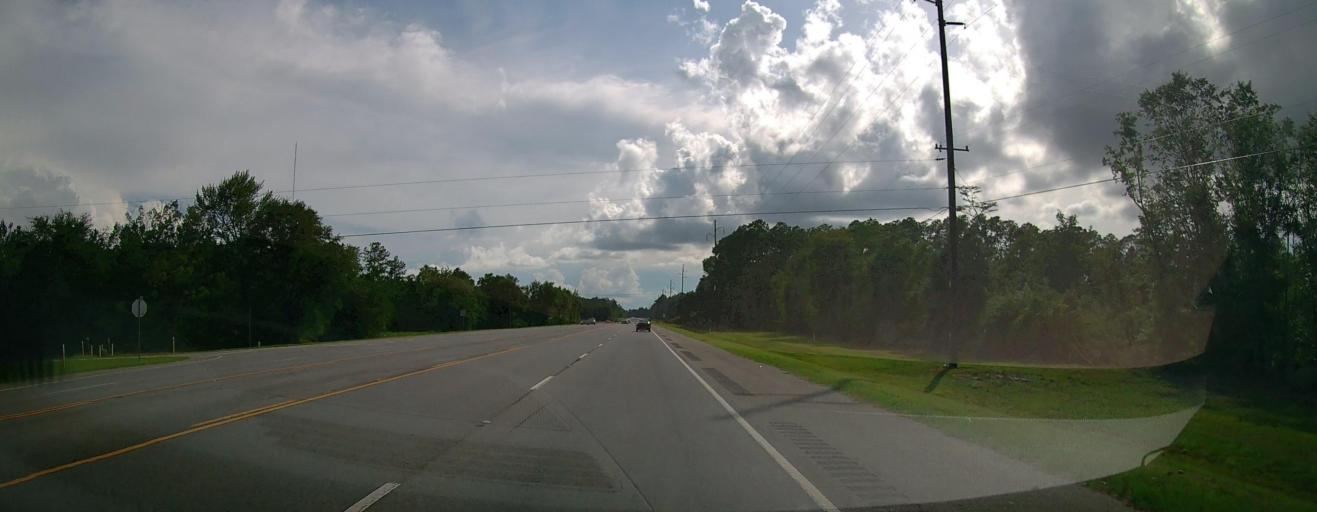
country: US
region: Georgia
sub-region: Wayne County
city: Jesup
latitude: 31.5991
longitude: -81.9335
